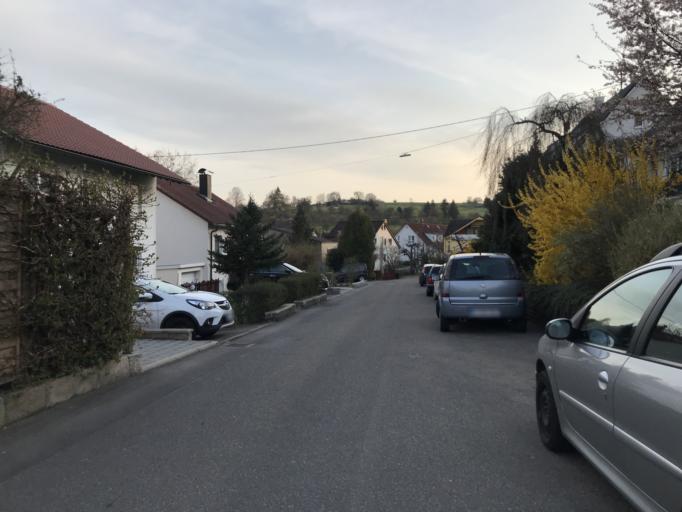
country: DE
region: Baden-Wuerttemberg
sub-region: Regierungsbezirk Stuttgart
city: Unterensingen
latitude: 48.6538
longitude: 9.3522
